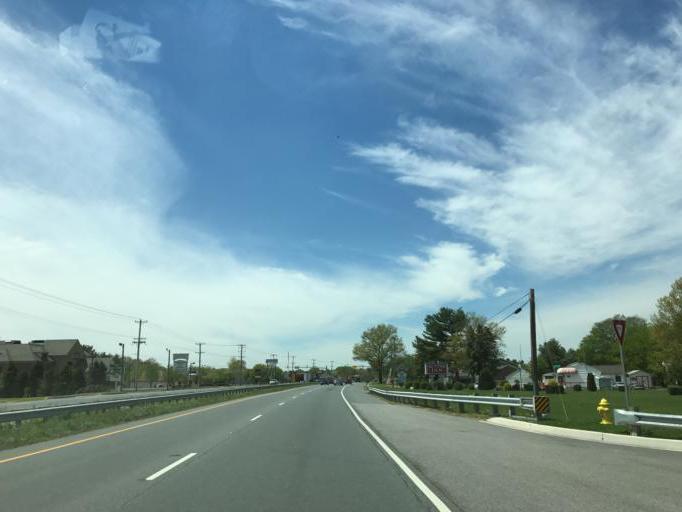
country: US
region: Maryland
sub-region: Cecil County
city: Elkton
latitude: 39.5988
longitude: -75.8123
